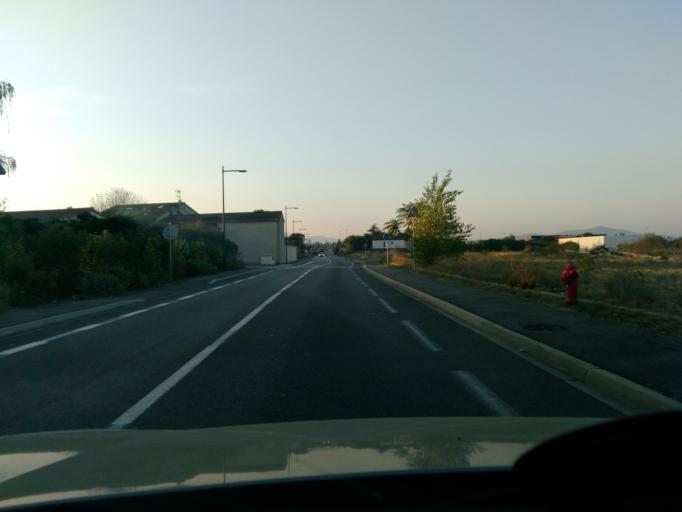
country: FR
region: Rhone-Alpes
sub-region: Departement de la Drome
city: Montelimar
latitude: 44.5336
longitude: 4.7515
